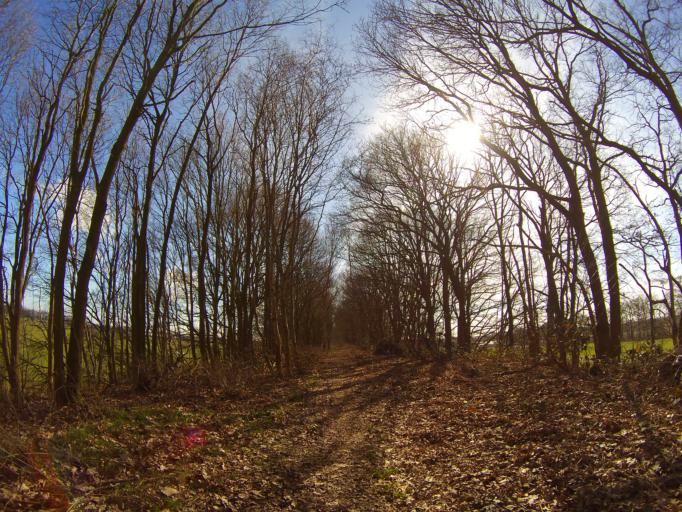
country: NL
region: Utrecht
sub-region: Gemeente Utrechtse Heuvelrug
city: Overberg
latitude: 52.0580
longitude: 5.4705
